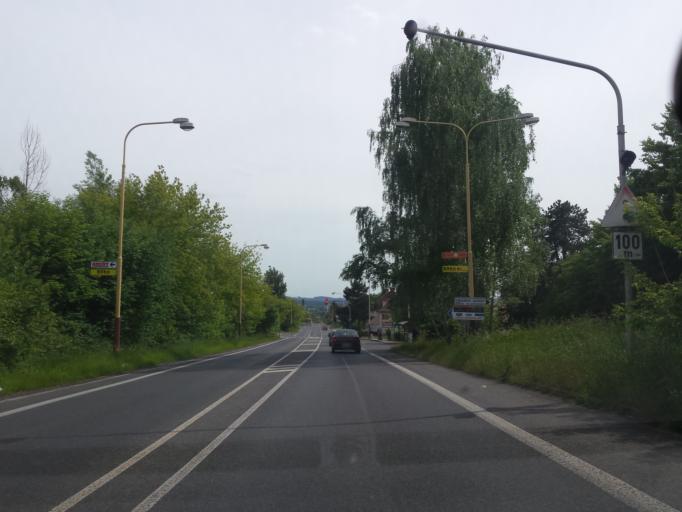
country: CZ
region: Liberecky
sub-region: Okres Ceska Lipa
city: Ceska Lipa
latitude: 50.6957
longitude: 14.5412
